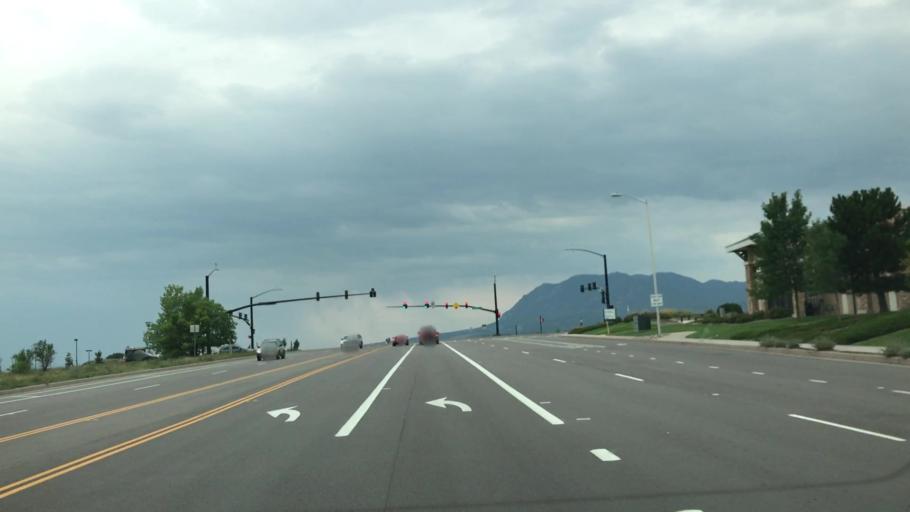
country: US
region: Colorado
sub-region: El Paso County
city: Colorado Springs
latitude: 38.8772
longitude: -104.8469
